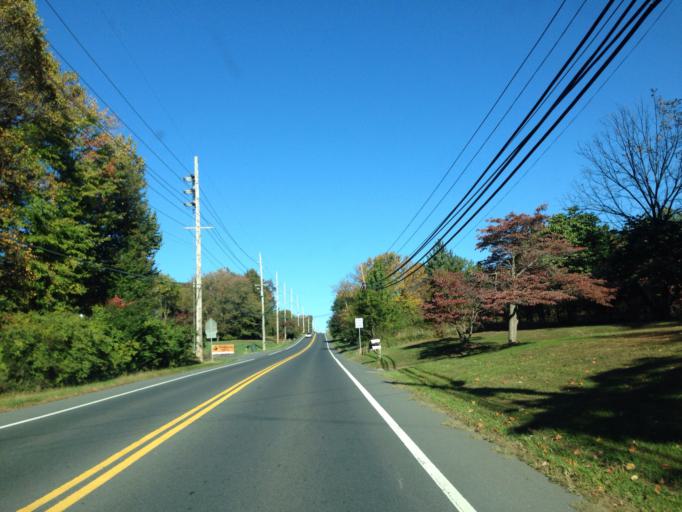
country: US
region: Maryland
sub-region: Montgomery County
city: Clarksburg
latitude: 39.2306
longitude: -77.2690
